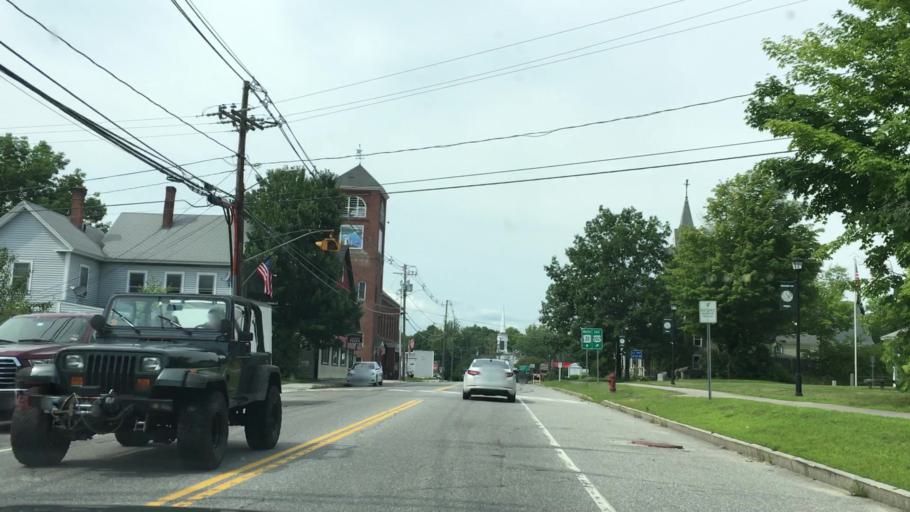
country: US
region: New Hampshire
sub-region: Hillsborough County
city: Antrim
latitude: 43.0290
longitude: -71.9380
